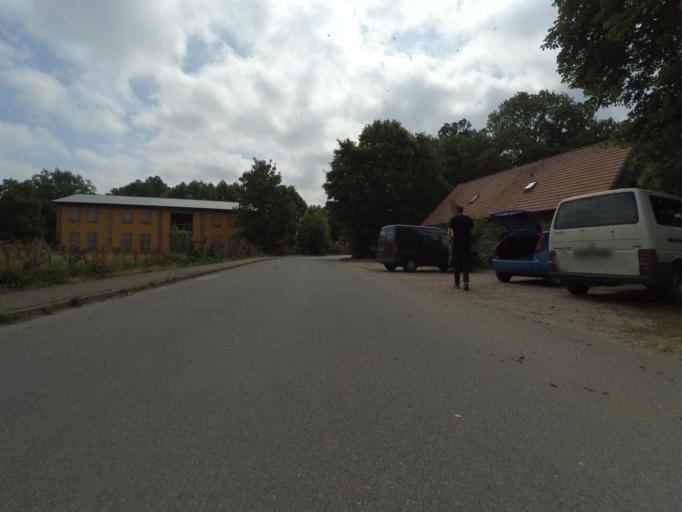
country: DE
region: Mecklenburg-Vorpommern
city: Krakow am See
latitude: 53.6065
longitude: 12.3849
